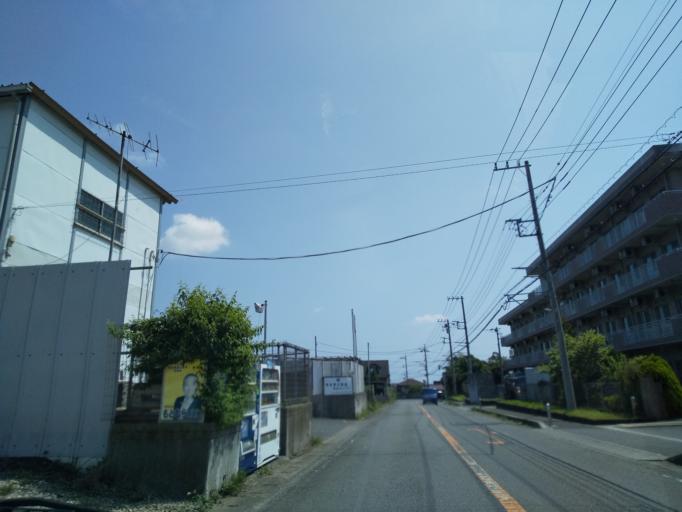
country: JP
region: Kanagawa
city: Zama
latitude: 35.5114
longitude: 139.3913
